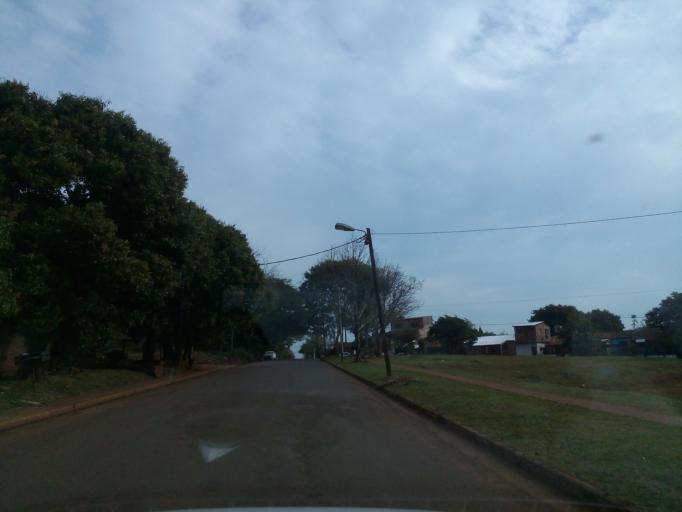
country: AR
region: Misiones
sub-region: Departamento de Capital
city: Posadas
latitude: -27.4243
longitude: -55.8838
